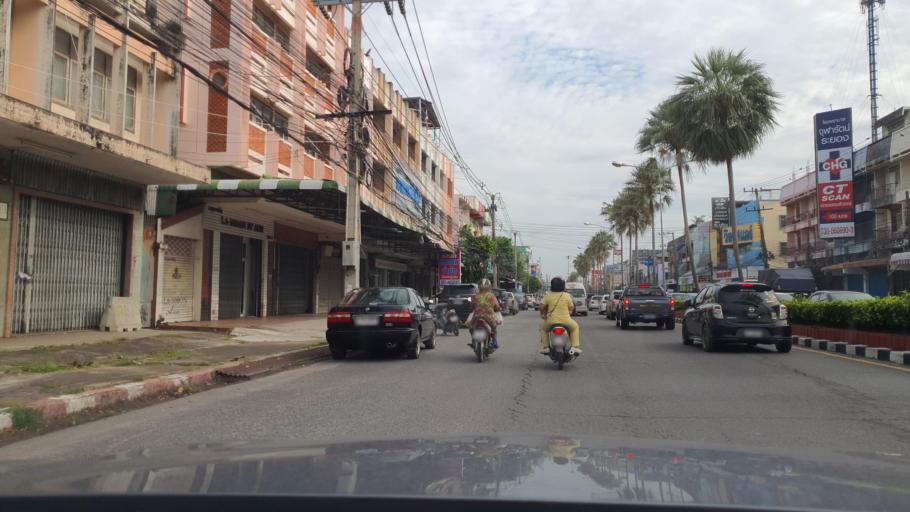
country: TH
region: Rayong
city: Rayong
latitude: 12.6849
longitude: 101.2752
